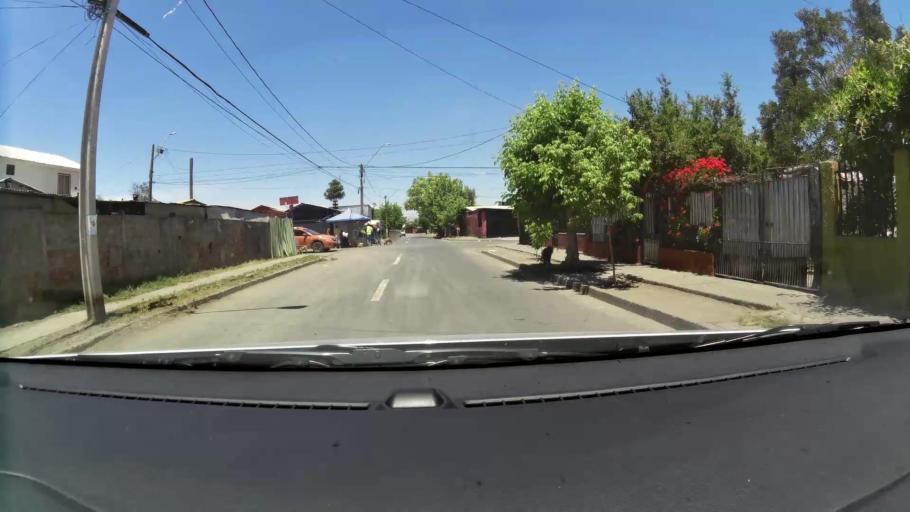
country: CL
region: Santiago Metropolitan
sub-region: Provincia de Santiago
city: La Pintana
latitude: -33.5592
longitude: -70.6427
